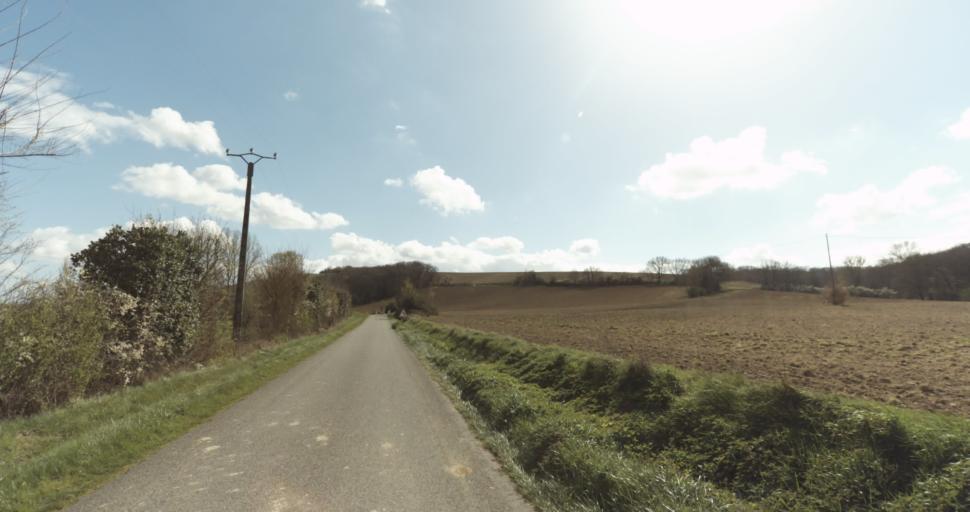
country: FR
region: Midi-Pyrenees
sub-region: Departement de la Haute-Garonne
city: Auterive
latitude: 43.3731
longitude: 1.5138
